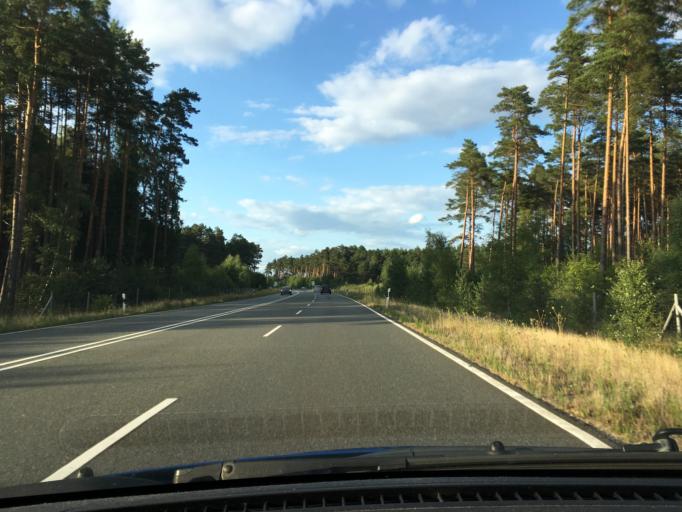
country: DE
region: Lower Saxony
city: Adelheidsdorf
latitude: 52.5654
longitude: 10.0761
